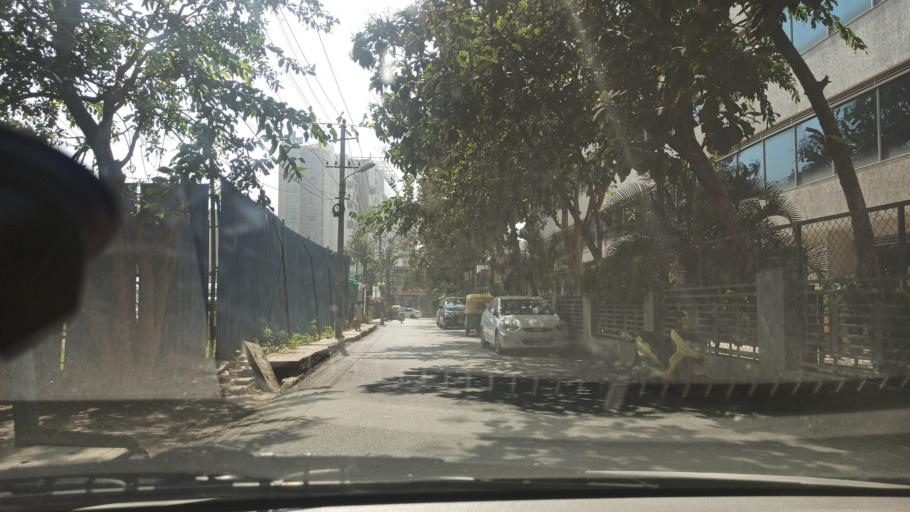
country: IN
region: Karnataka
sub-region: Bangalore Urban
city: Bangalore
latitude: 12.9325
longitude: 77.6863
